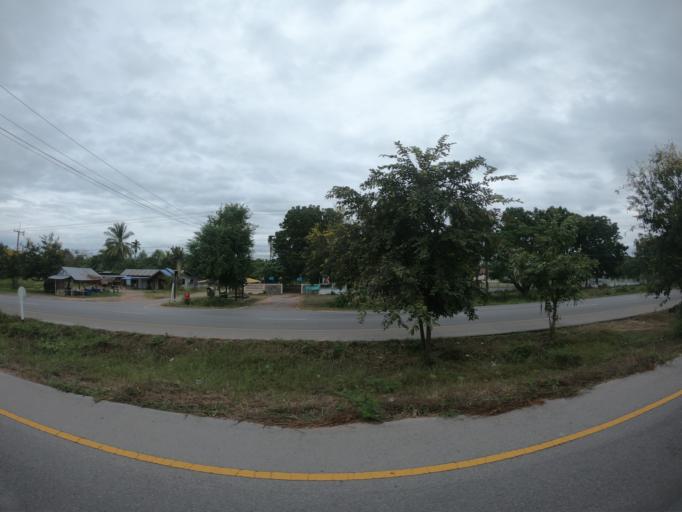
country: TH
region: Kalasin
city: Khong Chai
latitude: 16.1431
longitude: 103.4206
